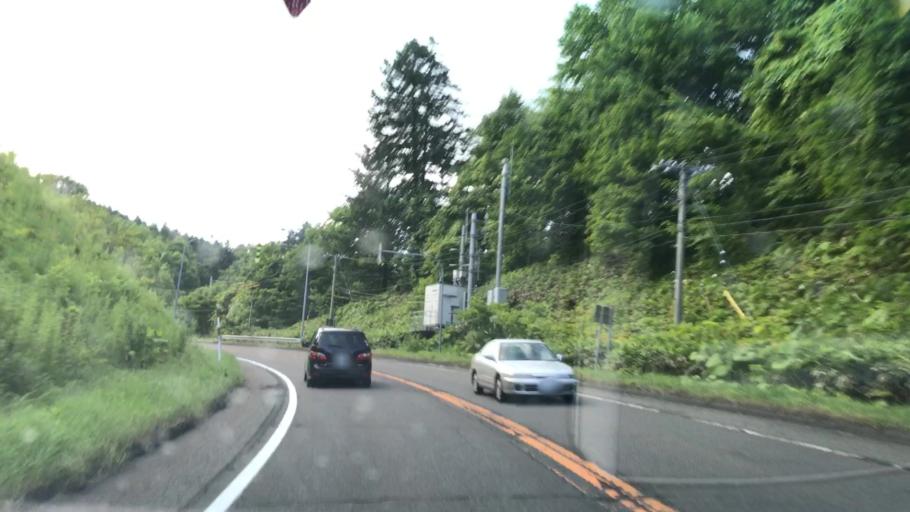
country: JP
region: Hokkaido
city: Shimo-furano
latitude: 42.9147
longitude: 142.4095
